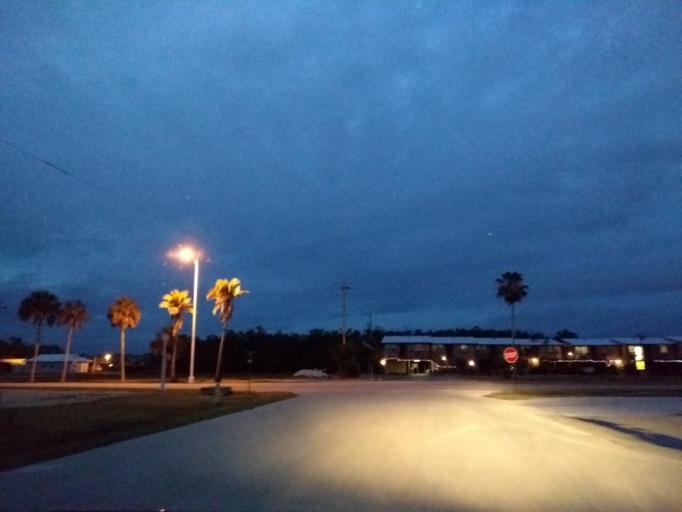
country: US
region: Florida
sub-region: Collier County
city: Marco
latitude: 25.8596
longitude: -81.3835
